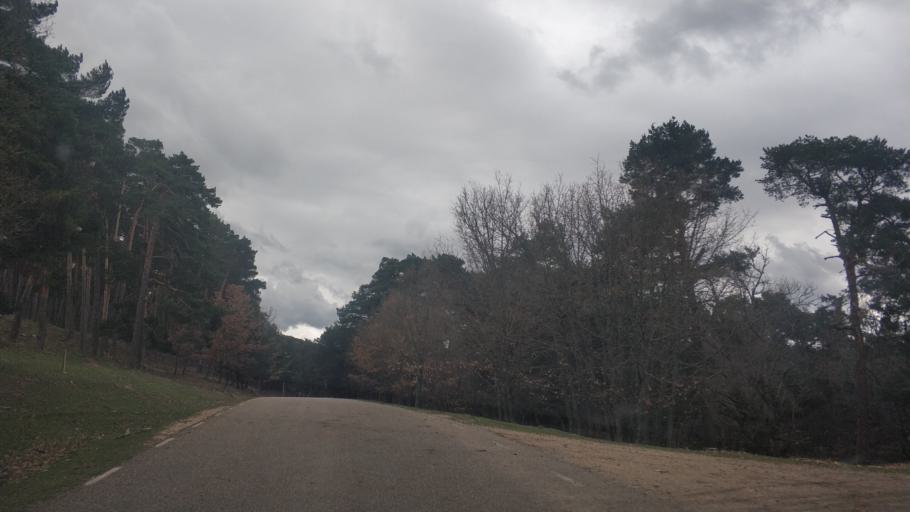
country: ES
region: Castille and Leon
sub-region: Provincia de Burgos
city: Canicosa de la Sierra
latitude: 41.9272
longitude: -3.0409
